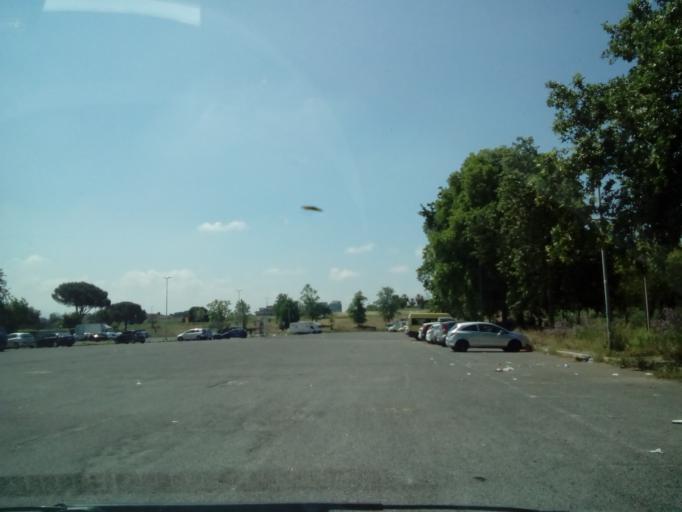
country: IT
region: Latium
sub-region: Citta metropolitana di Roma Capitale
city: Rome
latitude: 41.8822
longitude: 12.5845
